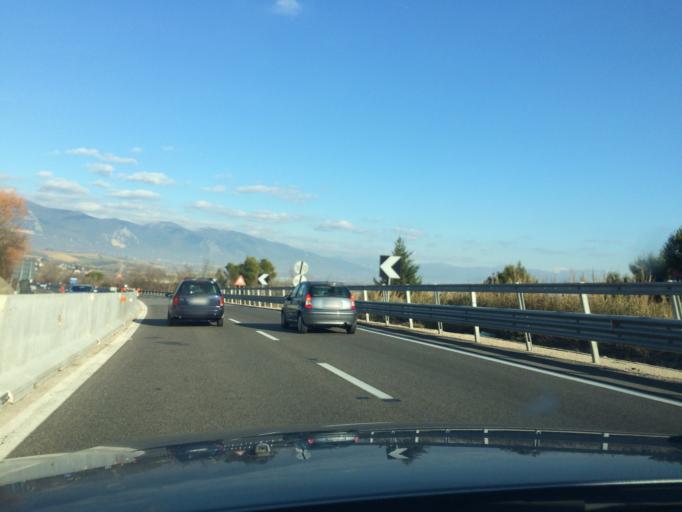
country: IT
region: Umbria
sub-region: Provincia di Terni
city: Narni Scalo
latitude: 42.5413
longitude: 12.5162
